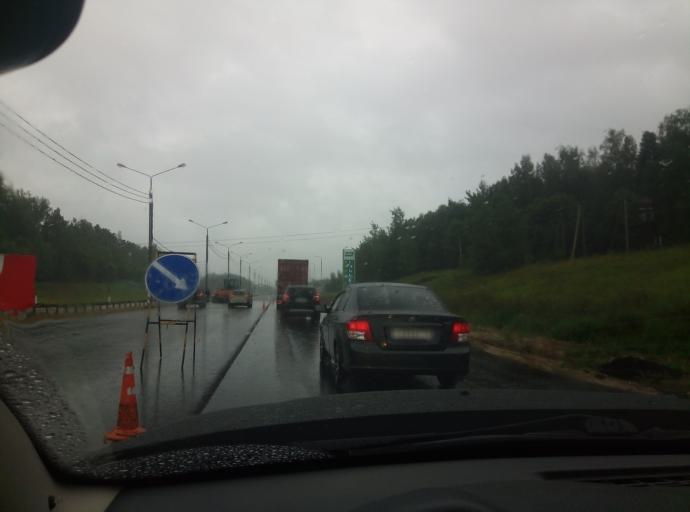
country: RU
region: Tula
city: Leninskiy
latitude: 54.4174
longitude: 37.5016
